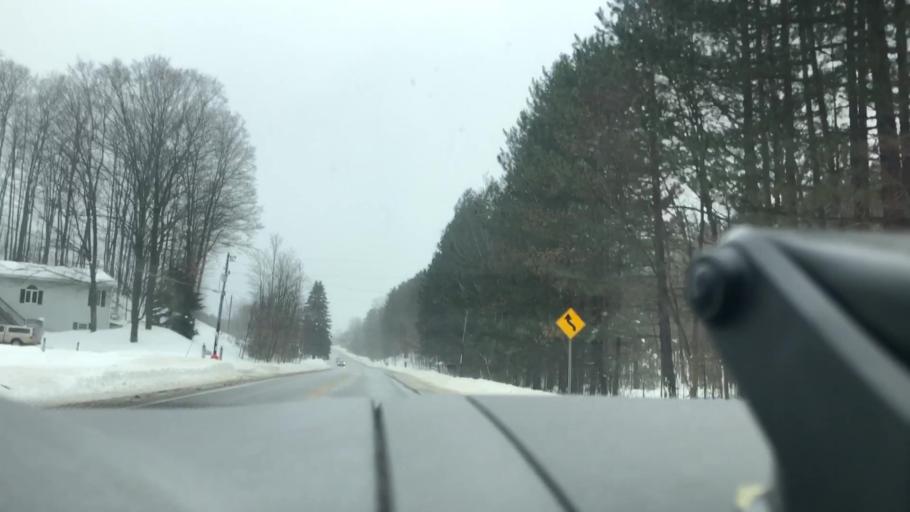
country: US
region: Michigan
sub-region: Charlevoix County
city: East Jordan
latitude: 45.1564
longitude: -85.1549
